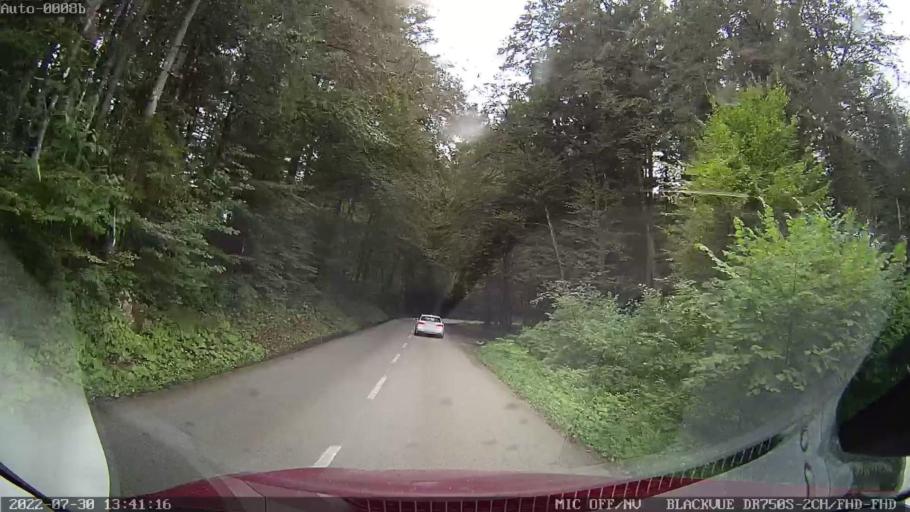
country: SI
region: Ivancna Gorica
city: Sentvid pri Sticni
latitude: 45.9027
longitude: 14.8990
